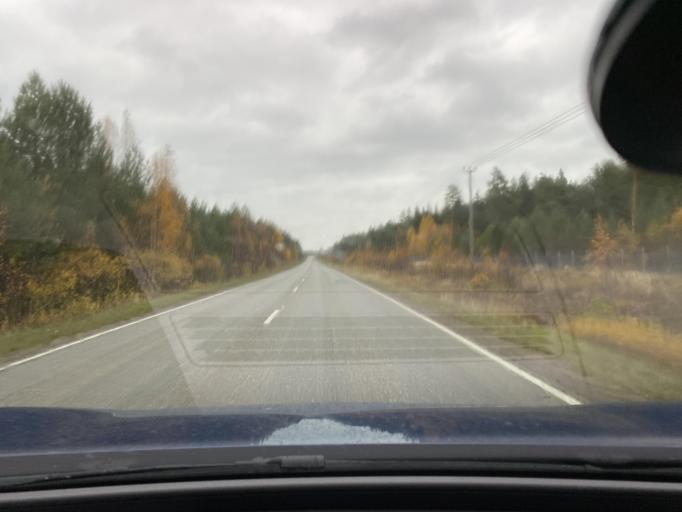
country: FI
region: Satakunta
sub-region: Rauma
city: Saekylae
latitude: 61.0493
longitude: 22.4342
